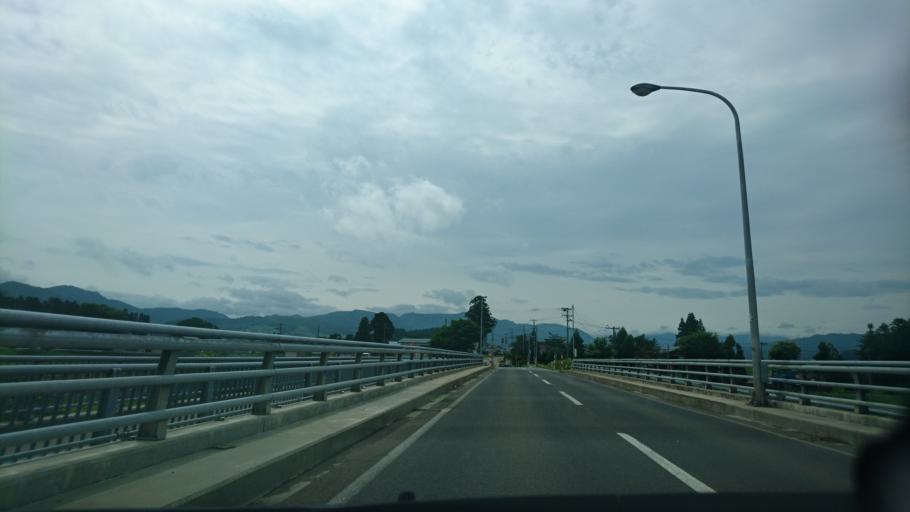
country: JP
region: Akita
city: Yuzawa
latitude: 39.1927
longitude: 140.5489
